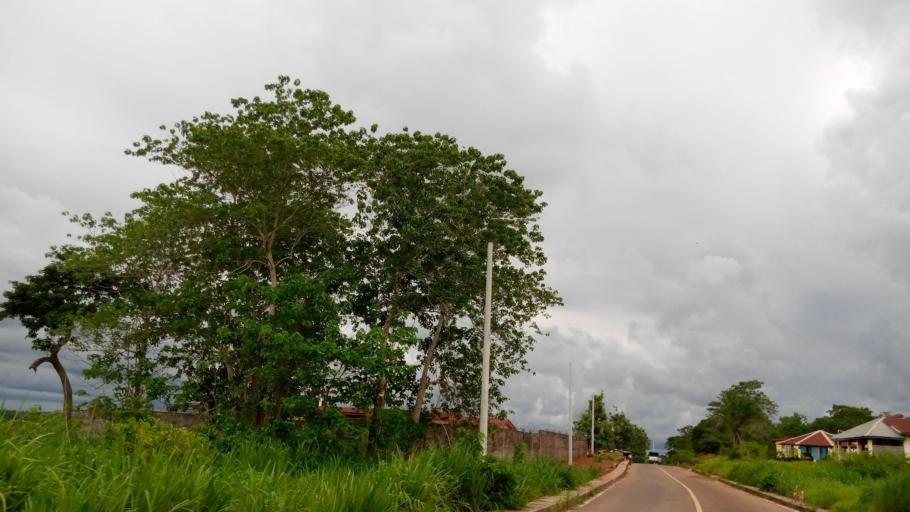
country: SL
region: Southern Province
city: Moyamba
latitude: 8.1617
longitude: -12.4486
